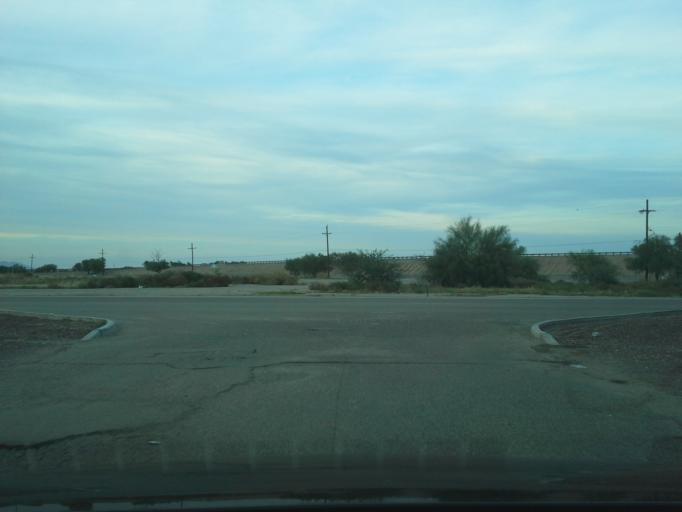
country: US
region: Arizona
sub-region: Pima County
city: Marana
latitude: 32.4603
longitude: -111.2179
